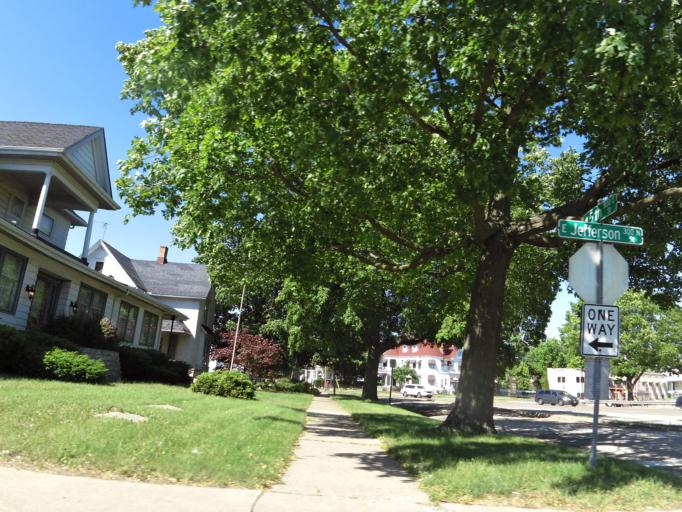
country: US
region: Illinois
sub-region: Winnebago County
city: Rockford
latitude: 42.2678
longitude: -89.0823
